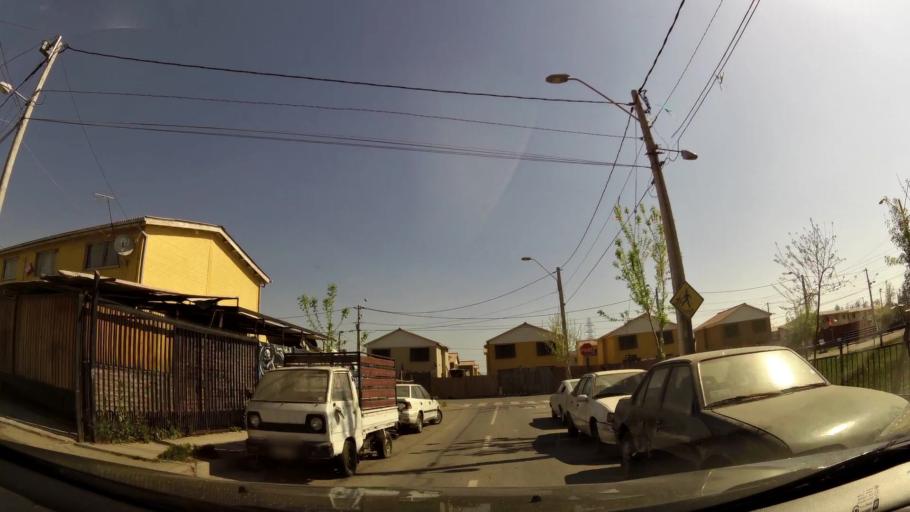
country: CL
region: Santiago Metropolitan
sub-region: Provincia de Santiago
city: La Pintana
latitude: -33.6331
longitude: -70.6272
